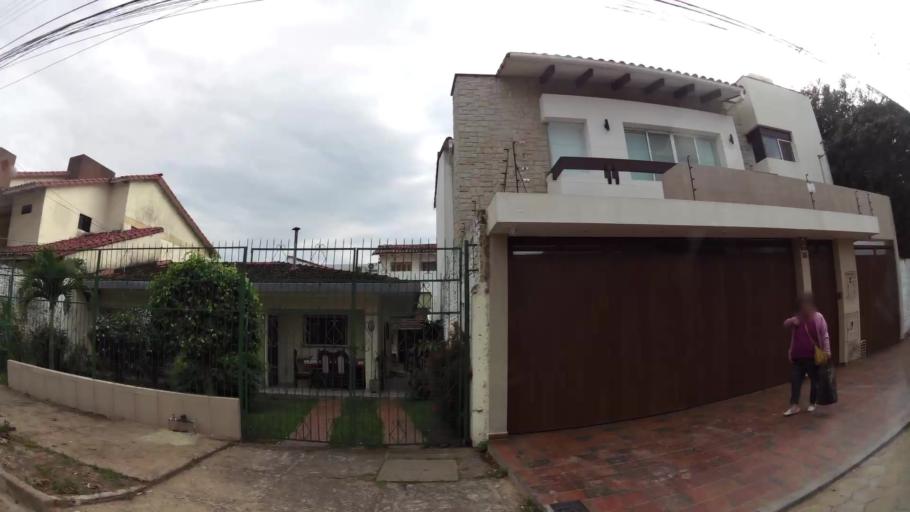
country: BO
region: Santa Cruz
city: Santa Cruz de la Sierra
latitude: -17.7529
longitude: -63.1682
